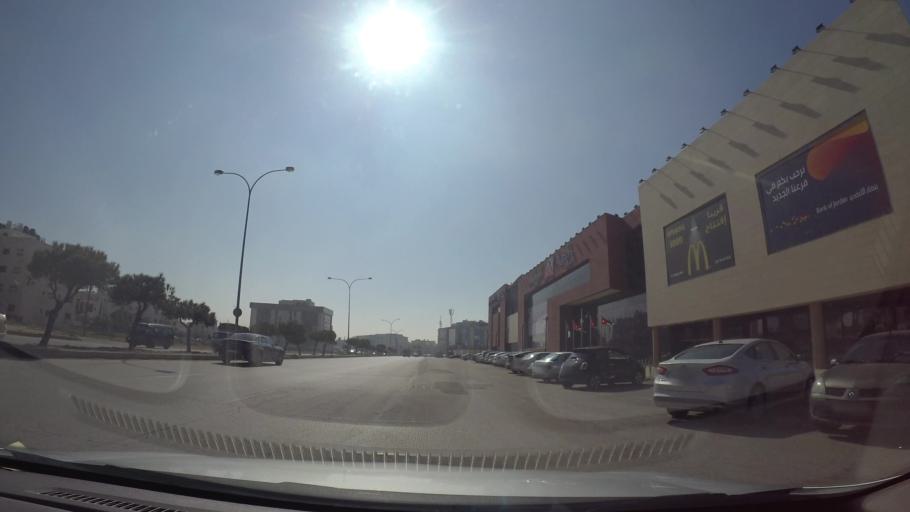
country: JO
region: Amman
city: Al Bunayyat ash Shamaliyah
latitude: 31.9047
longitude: 35.8874
